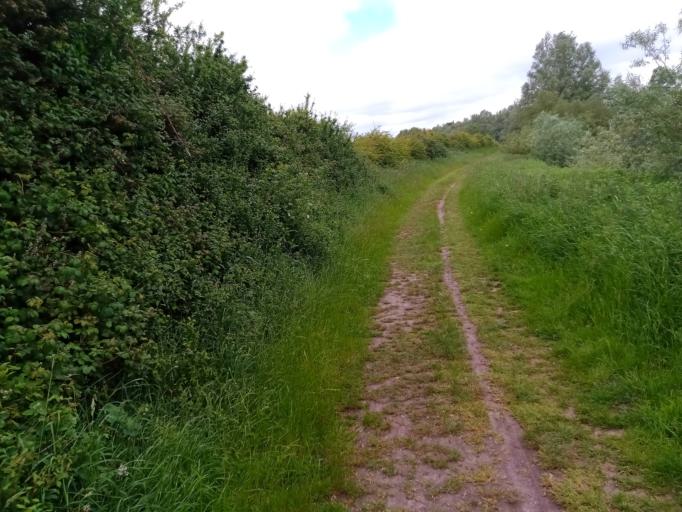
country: IE
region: Leinster
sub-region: County Carlow
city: Carlow
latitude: 52.8254
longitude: -6.9406
